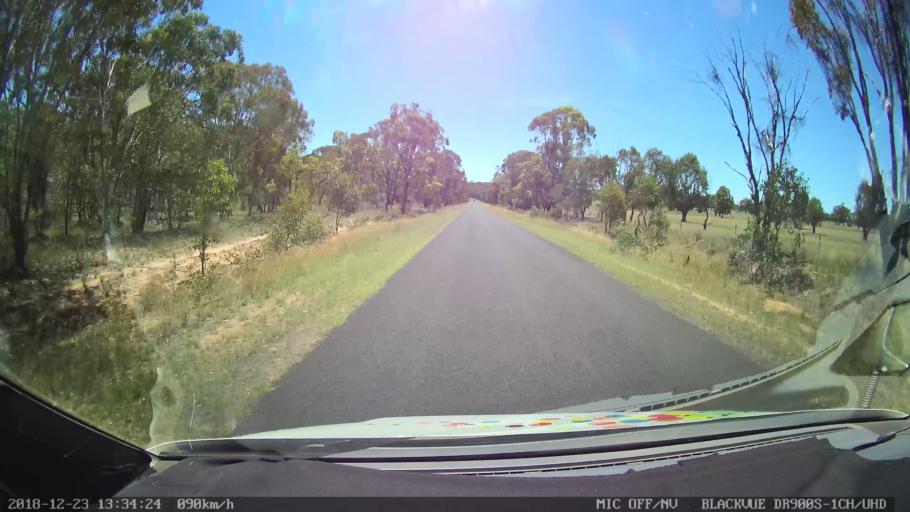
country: AU
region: New South Wales
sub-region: Armidale Dumaresq
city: Armidale
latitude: -30.4497
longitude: 151.2656
